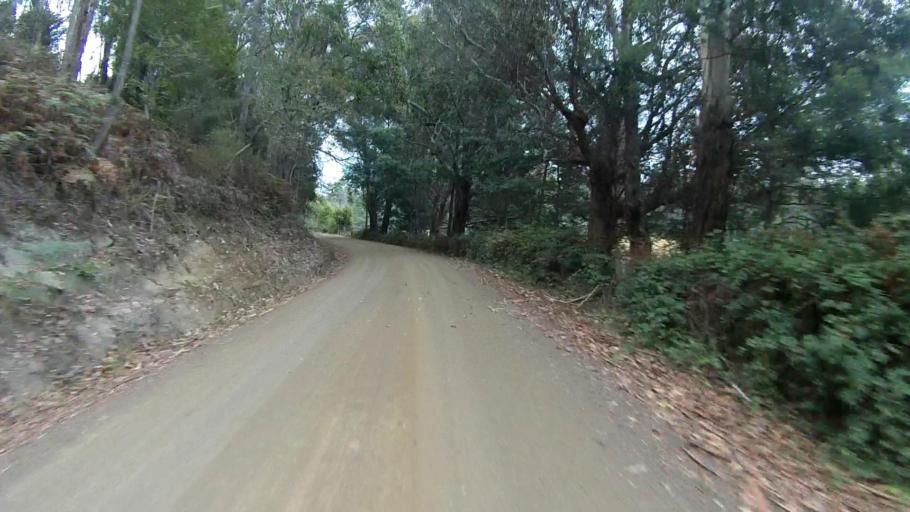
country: AU
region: Tasmania
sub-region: Huon Valley
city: Cygnet
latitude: -43.2307
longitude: 147.1597
